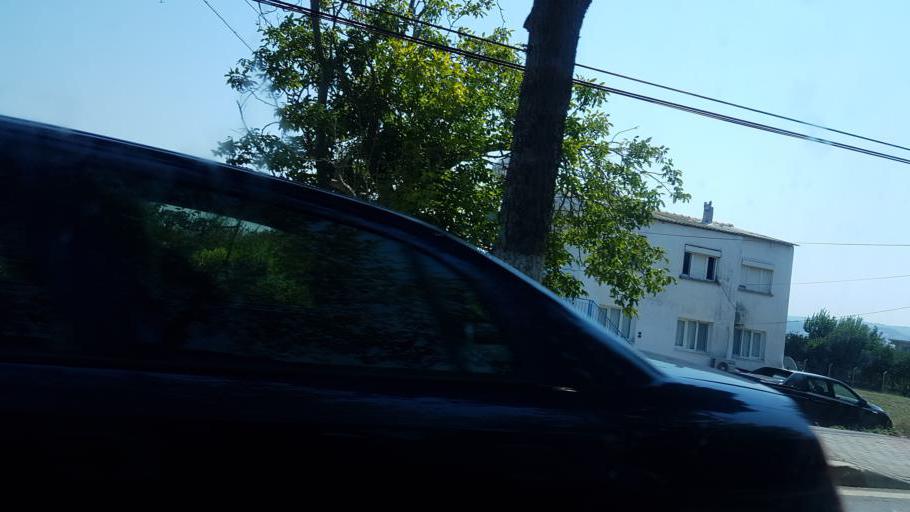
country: TR
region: Izmir
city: Urla
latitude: 38.3496
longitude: 26.7717
